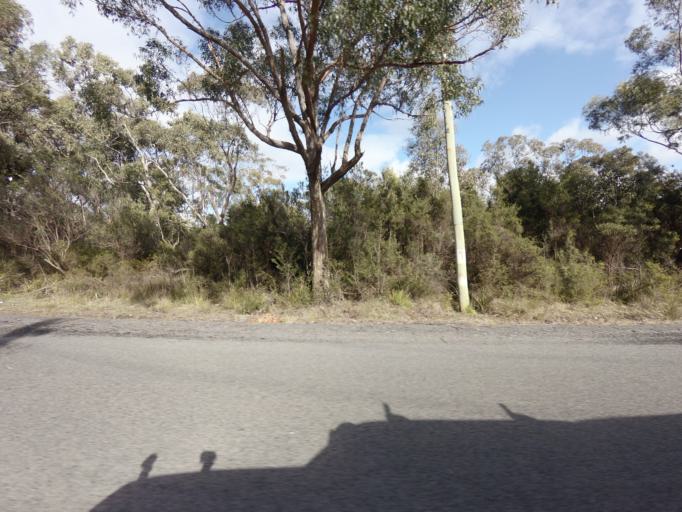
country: AU
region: Tasmania
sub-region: Huon Valley
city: Geeveston
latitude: -43.4371
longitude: 146.9038
